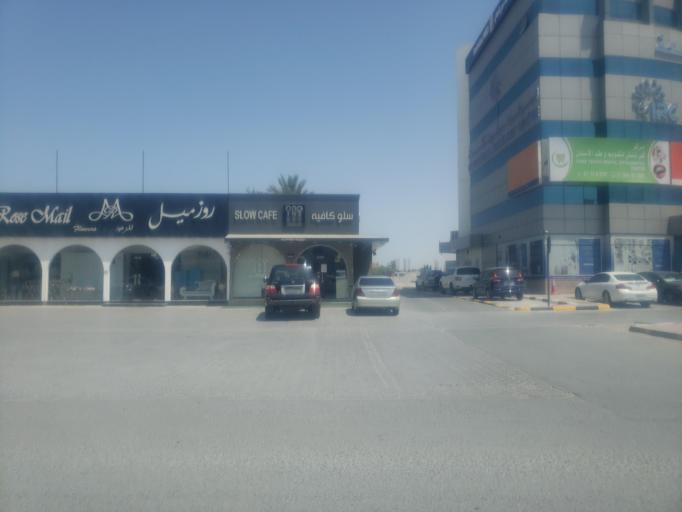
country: AE
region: Ra's al Khaymah
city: Ras al-Khaimah
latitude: 25.8019
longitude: 55.9740
